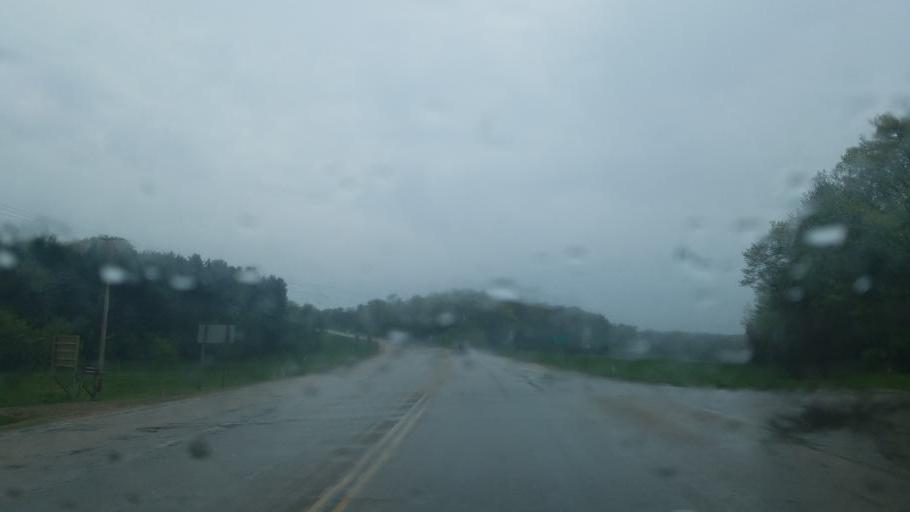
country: US
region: Wisconsin
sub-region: Sauk County
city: Reedsburg
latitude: 43.5939
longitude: -90.1267
